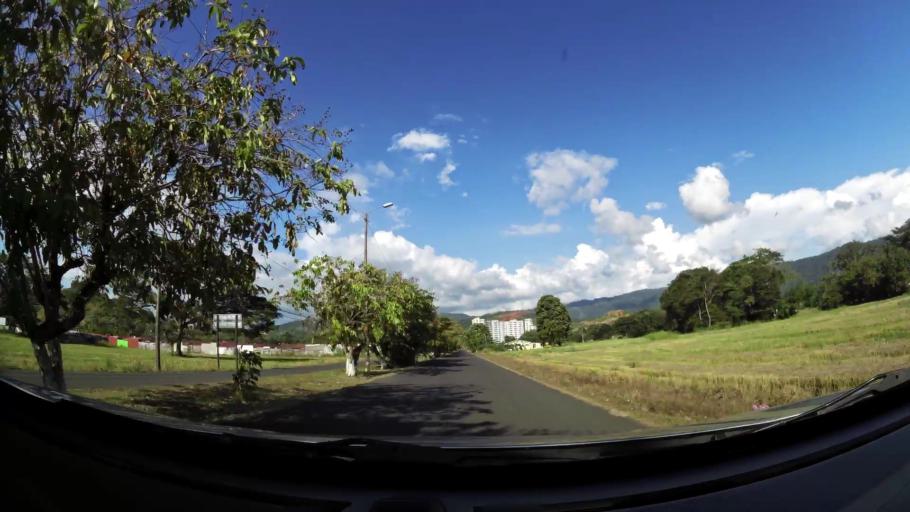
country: CR
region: Puntarenas
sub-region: Canton de Garabito
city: Jaco
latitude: 9.6277
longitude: -84.6330
